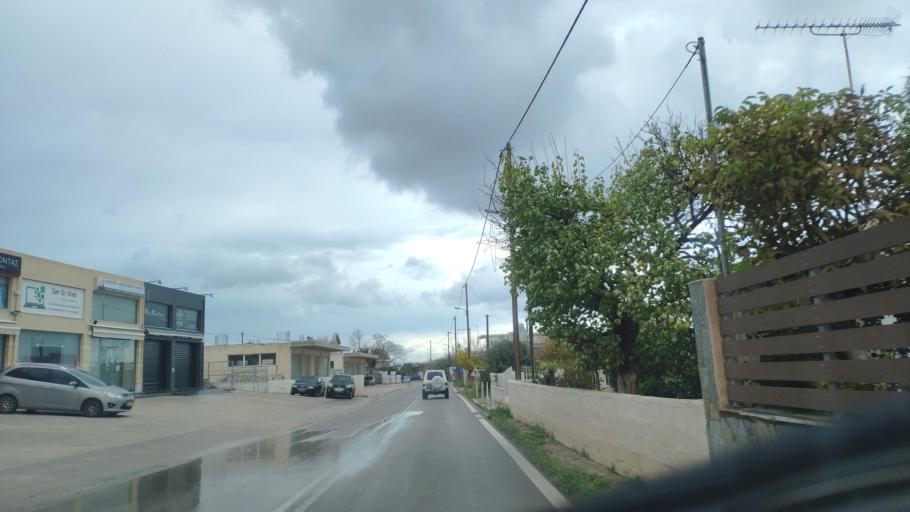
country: GR
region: Attica
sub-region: Nomarchia Anatolikis Attikis
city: Artemida
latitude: 37.9502
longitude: 24.0073
